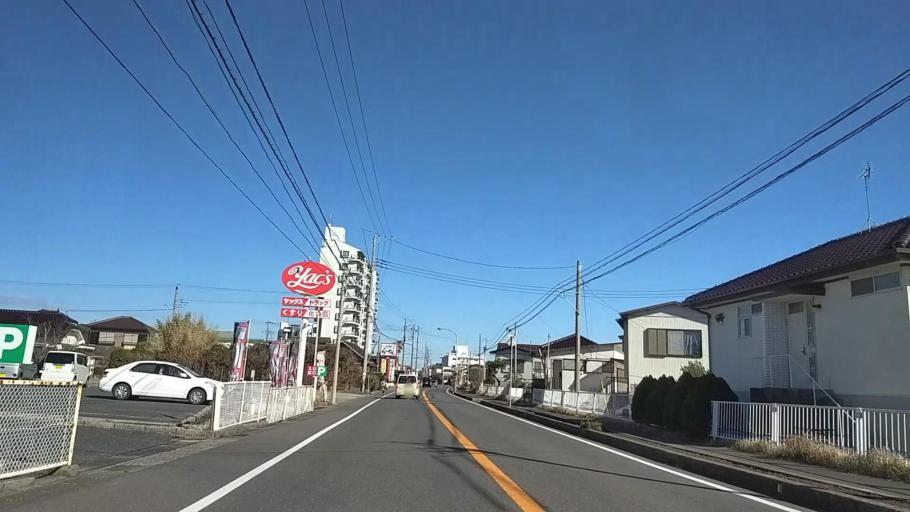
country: JP
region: Chiba
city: Tateyama
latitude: 34.9760
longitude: 139.9637
